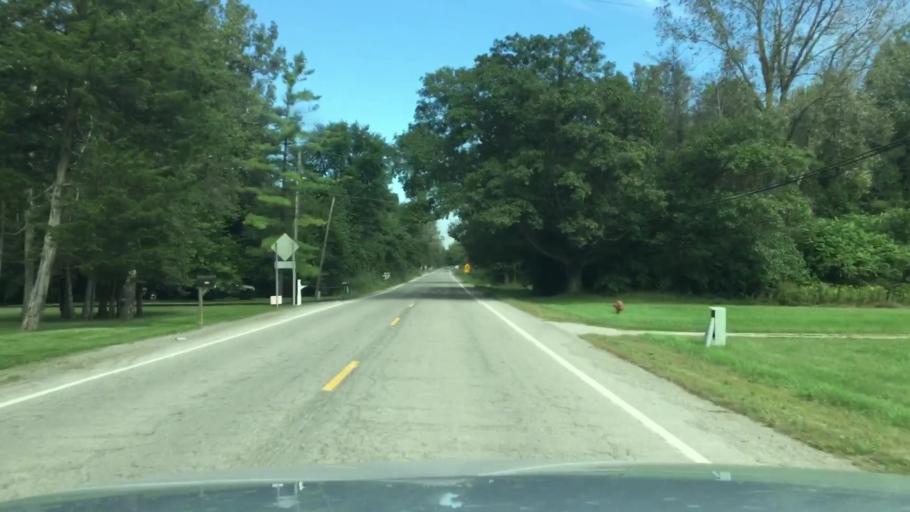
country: US
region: Michigan
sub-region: Wayne County
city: Belleville
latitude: 42.1570
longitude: -83.4613
